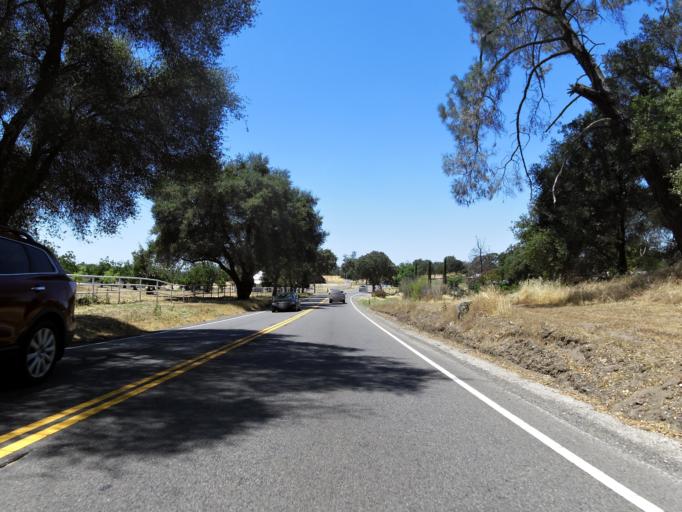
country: US
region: California
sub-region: Fresno County
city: Auberry
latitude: 37.0376
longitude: -119.5043
